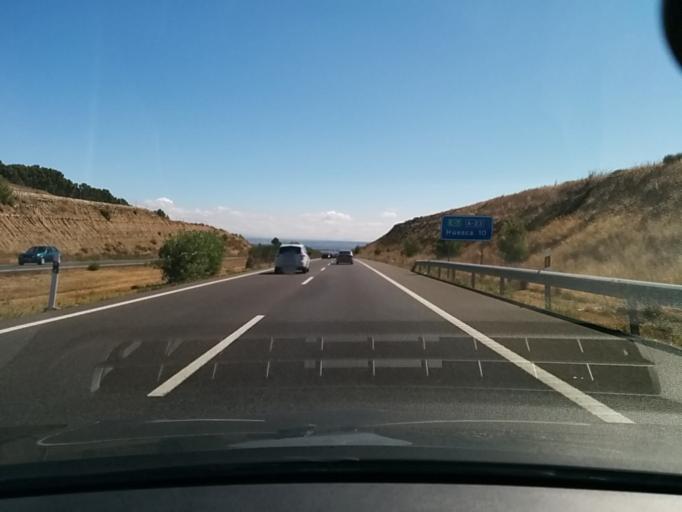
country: ES
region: Aragon
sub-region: Provincia de Huesca
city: Almudebar
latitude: 42.0699
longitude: -0.5100
